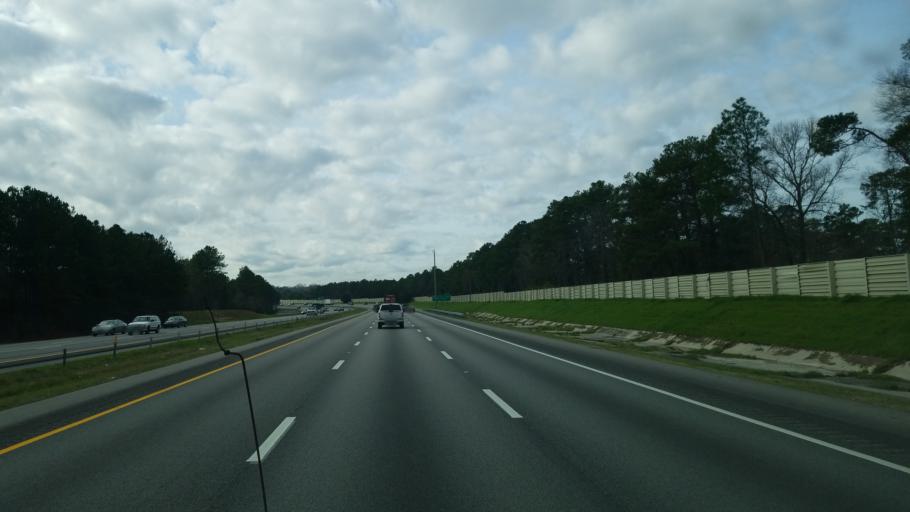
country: US
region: South Carolina
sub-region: Richland County
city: Forest Acres
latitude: 34.0037
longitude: -80.9582
